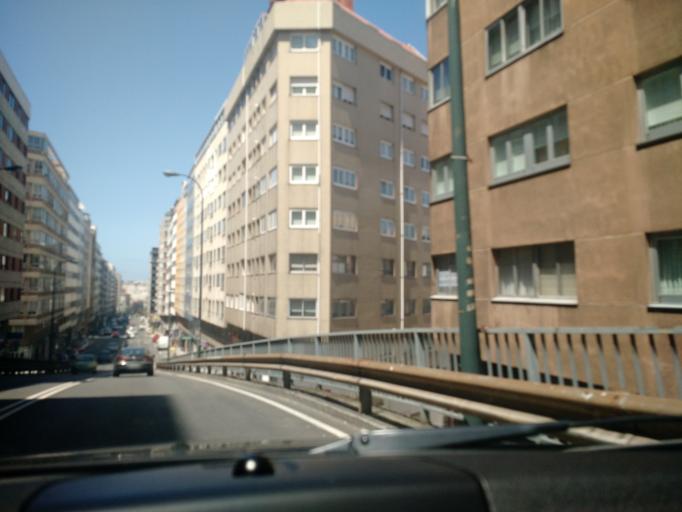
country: ES
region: Galicia
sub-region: Provincia da Coruna
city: A Coruna
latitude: 43.3615
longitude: -8.4155
